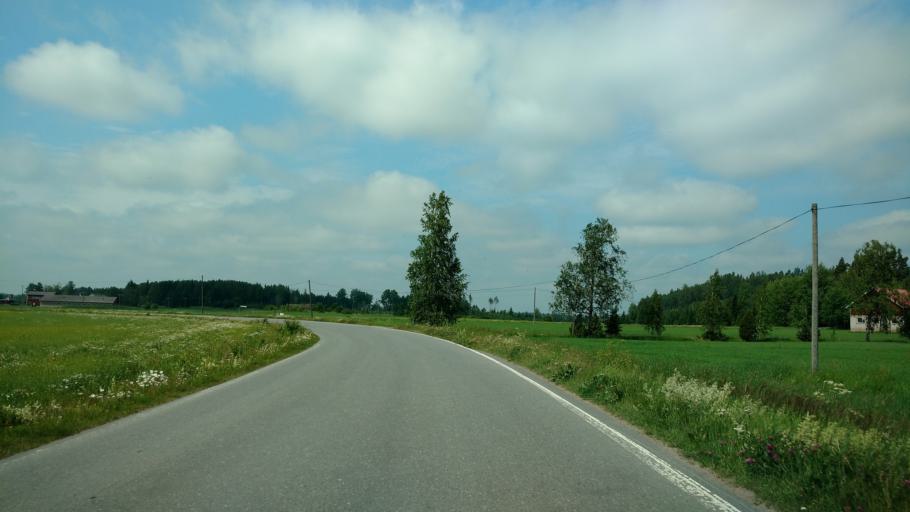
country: FI
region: Haeme
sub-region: Forssa
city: Jokioinen
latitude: 60.7899
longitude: 23.3851
